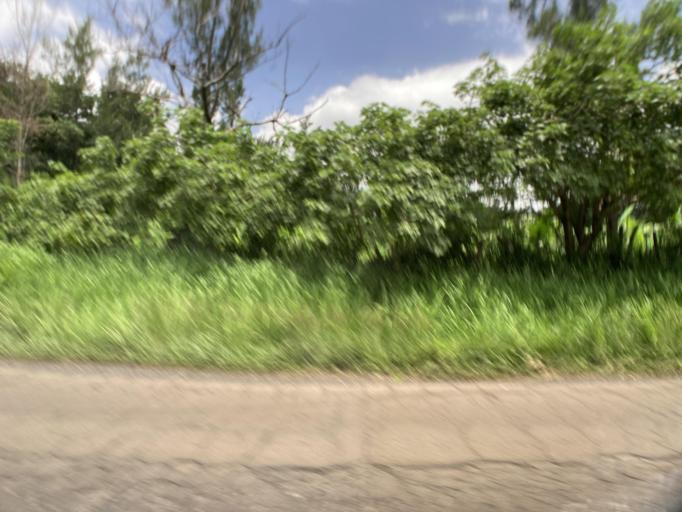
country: GT
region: Guatemala
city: Villa Canales
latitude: 14.4204
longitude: -90.5442
